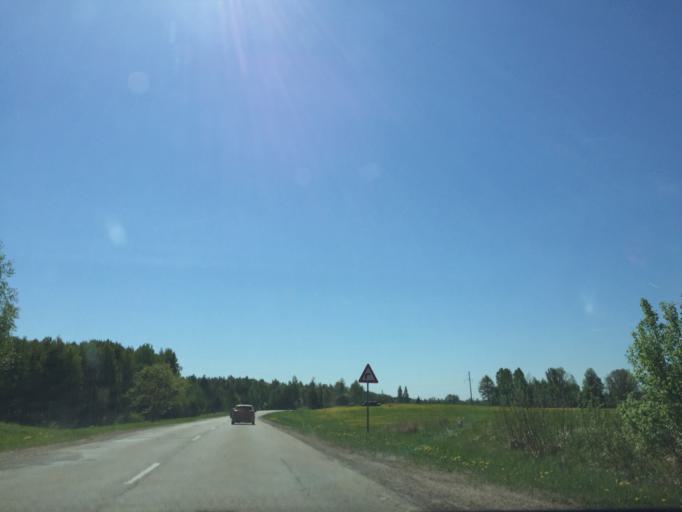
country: LV
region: Malpils
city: Malpils
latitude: 56.9283
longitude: 24.9360
